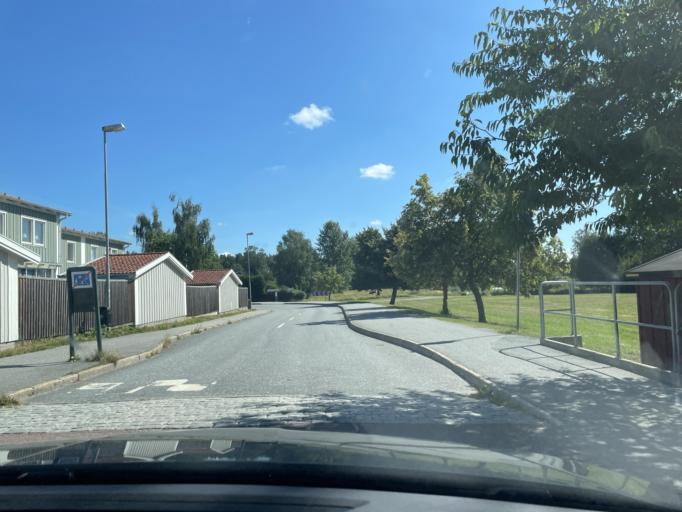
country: SE
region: Stockholm
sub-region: Sigtuna Kommun
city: Rosersberg
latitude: 59.5827
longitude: 17.8824
